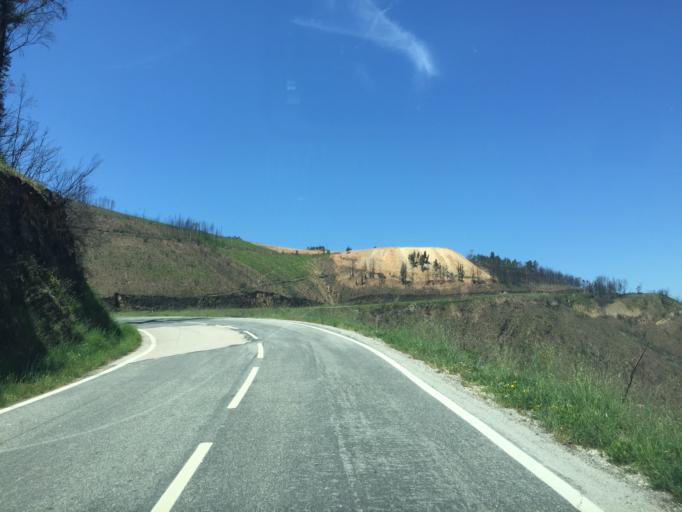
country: PT
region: Coimbra
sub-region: Pampilhosa da Serra
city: Pampilhosa da Serra
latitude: 40.0299
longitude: -7.9608
